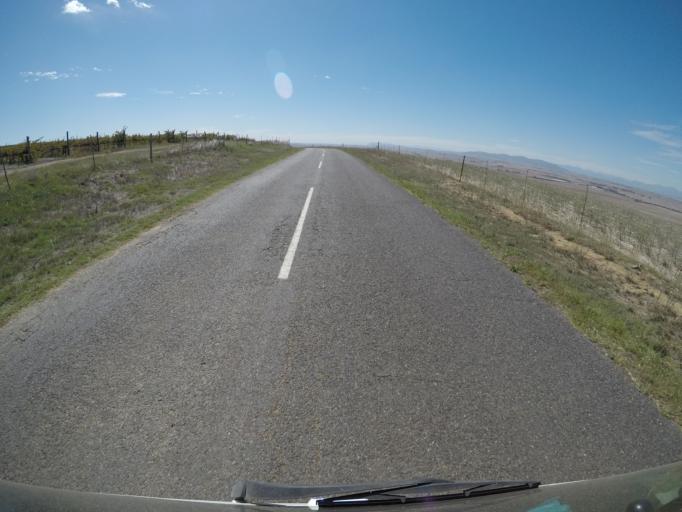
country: ZA
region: Western Cape
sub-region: City of Cape Town
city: Sunset Beach
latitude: -33.7161
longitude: 18.5822
